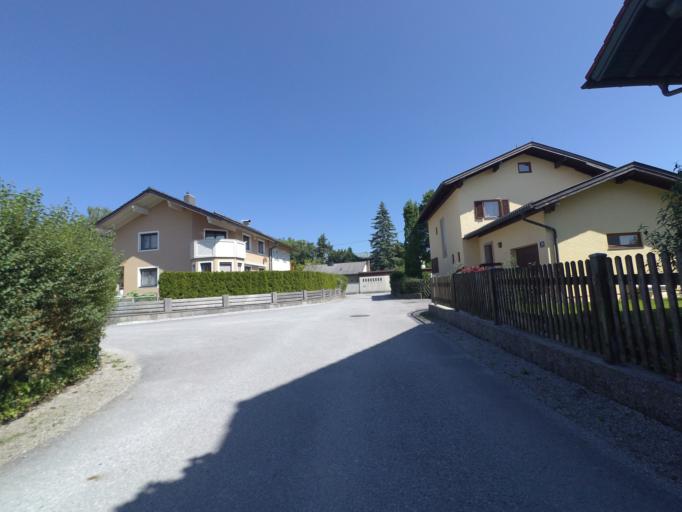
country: AT
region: Salzburg
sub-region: Politischer Bezirk Salzburg-Umgebung
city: Grodig
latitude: 47.7612
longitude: 13.0328
